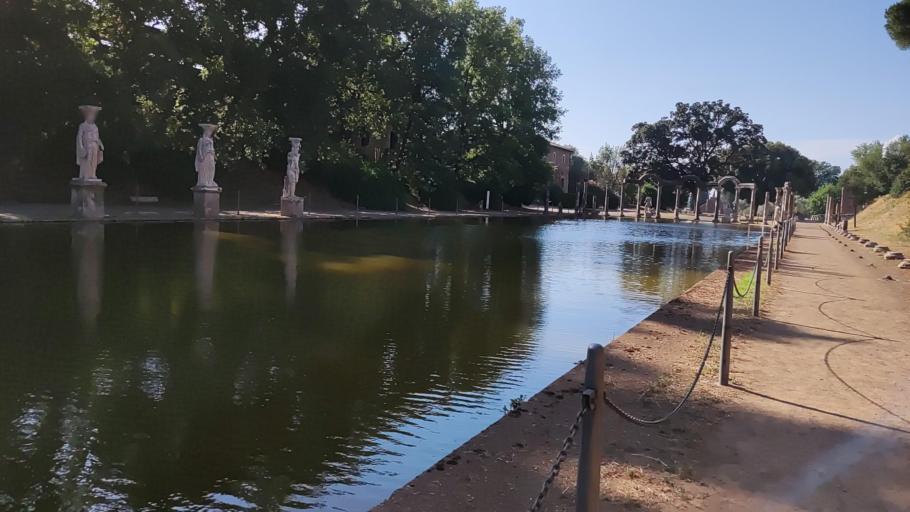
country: IT
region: Latium
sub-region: Citta metropolitana di Roma Capitale
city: Villa Adriana
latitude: 41.9384
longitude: 12.7761
